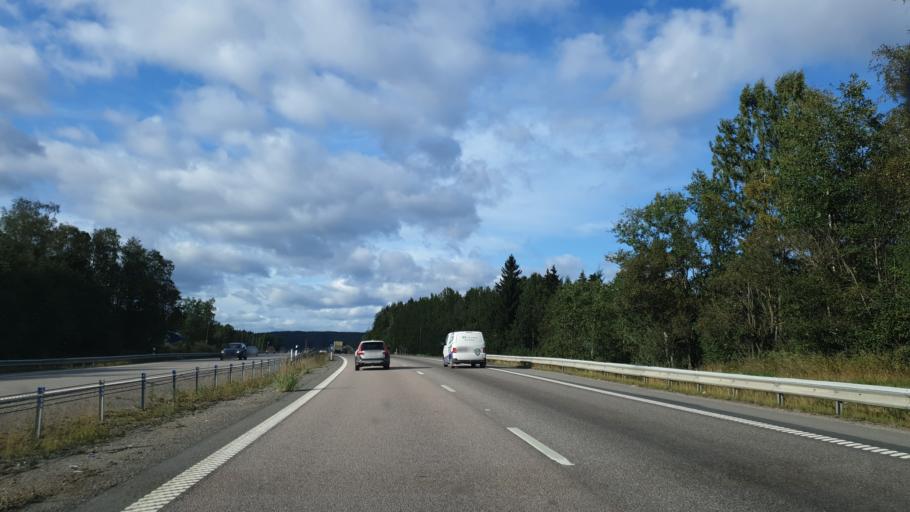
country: SE
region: Vaesternorrland
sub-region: Sundsvalls Kommun
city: Johannedal
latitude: 62.4276
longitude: 17.3486
